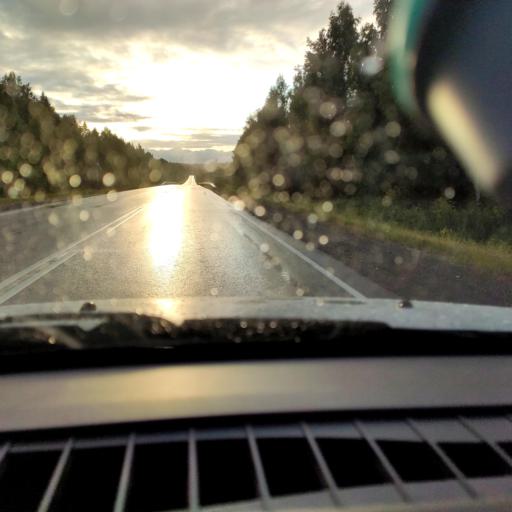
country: RU
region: Perm
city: Verkhnechusovskiye Gorodki
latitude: 58.2480
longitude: 57.0194
